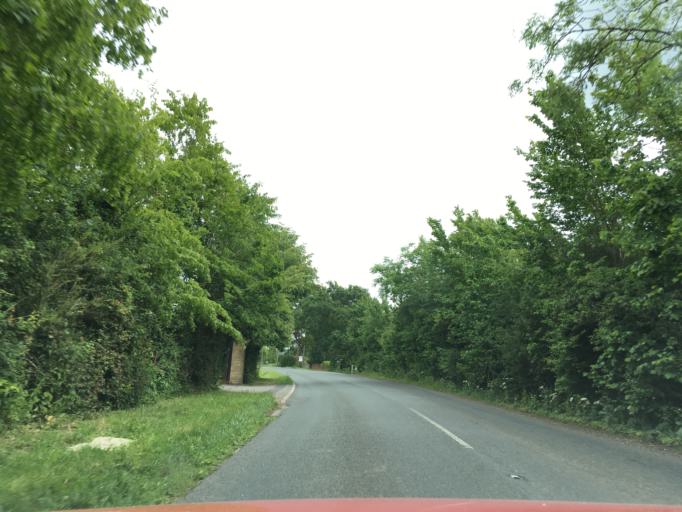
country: GB
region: England
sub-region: Wiltshire
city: Charlton
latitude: 51.5657
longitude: -2.0262
